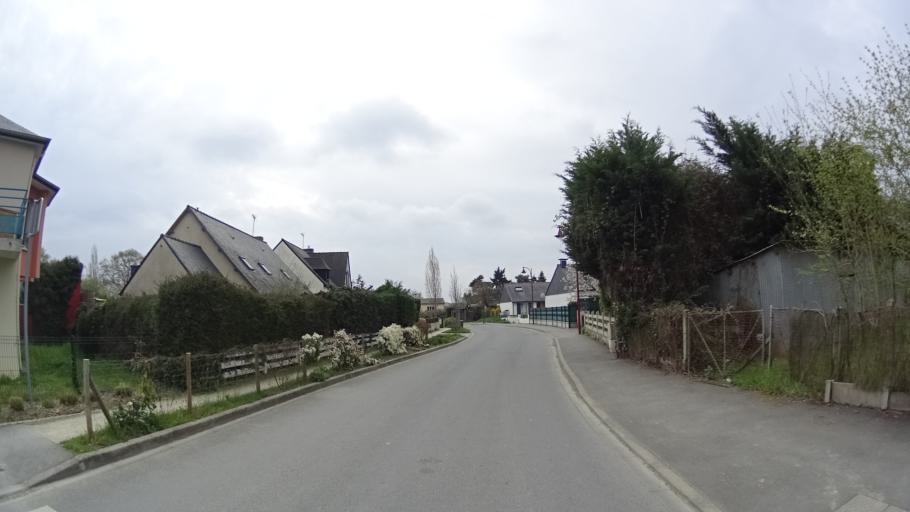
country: FR
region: Brittany
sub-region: Departement d'Ille-et-Vilaine
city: La Chapelle-Thouarault
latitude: 48.1230
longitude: -1.8653
